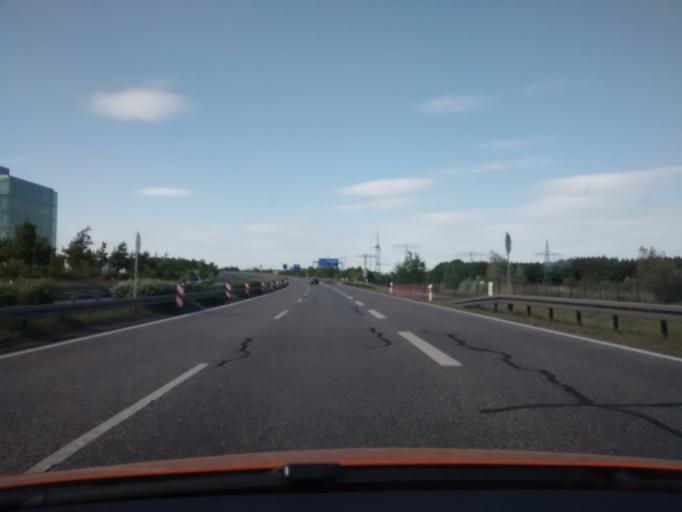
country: DE
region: Brandenburg
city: Ludwigsfelde
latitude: 52.3013
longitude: 13.2858
